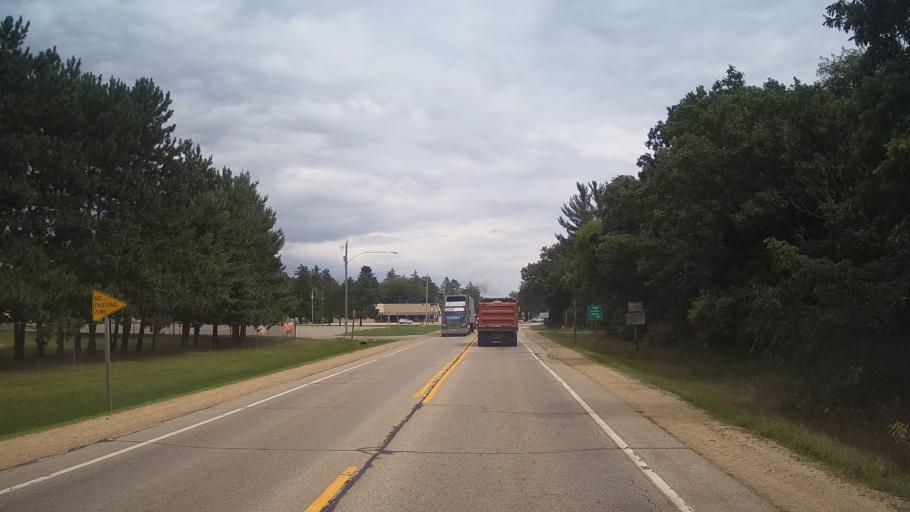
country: US
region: Wisconsin
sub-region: Waushara County
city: Wautoma
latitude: 44.0684
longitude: -89.3004
